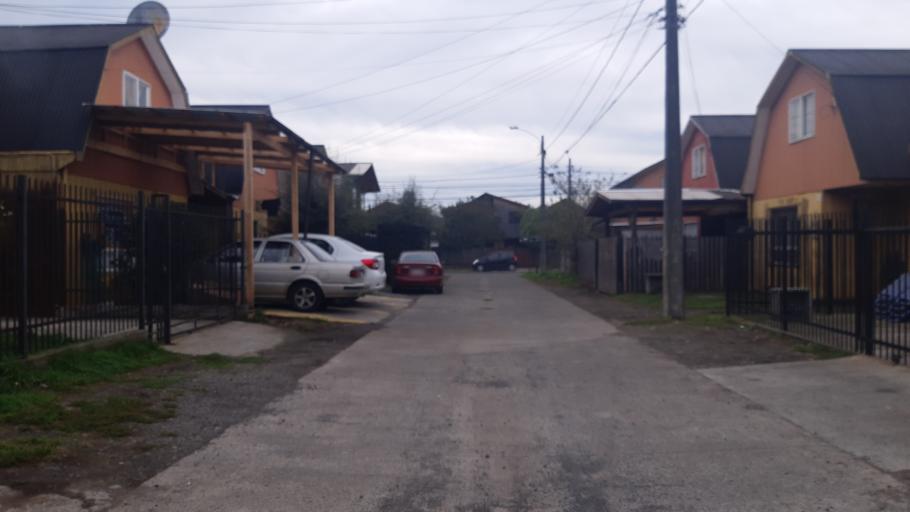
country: CL
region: Araucania
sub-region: Provincia de Cautin
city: Villarrica
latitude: -39.3077
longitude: -72.2164
